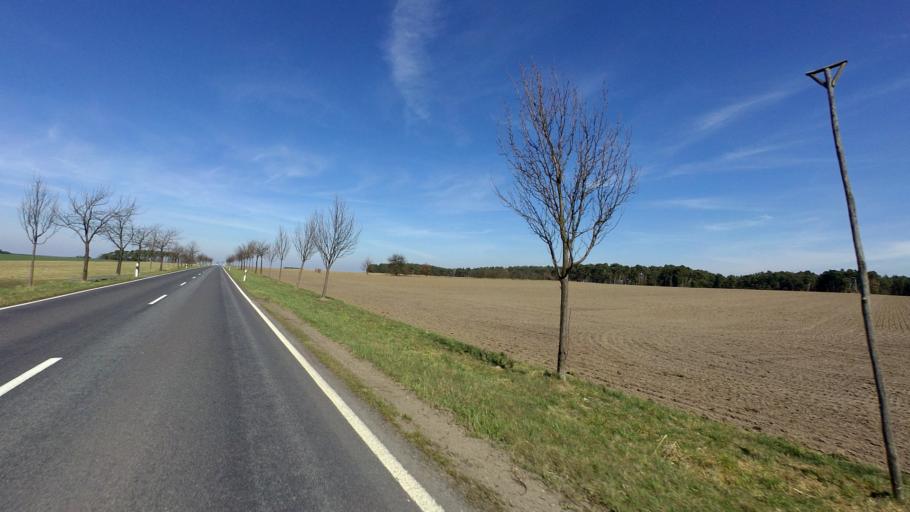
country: DE
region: Brandenburg
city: Munchehofe
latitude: 52.1656
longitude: 13.9208
